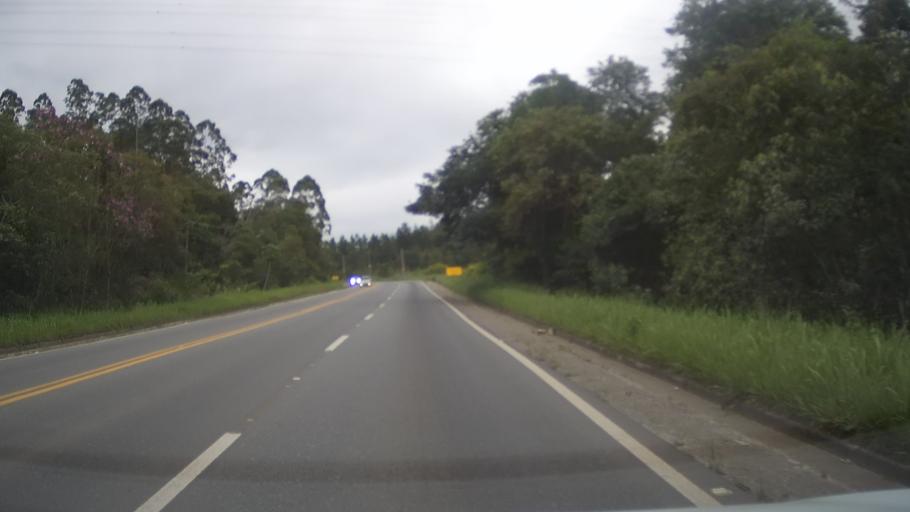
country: BR
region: Sao Paulo
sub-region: Aruja
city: Aruja
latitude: -23.3664
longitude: -46.4245
